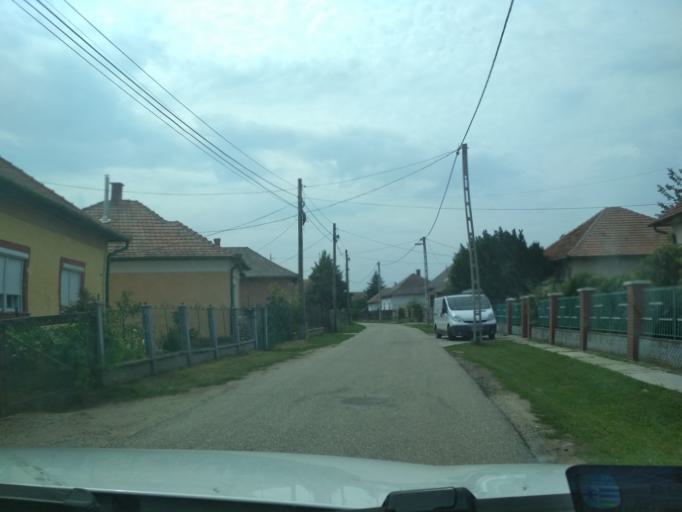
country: HU
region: Jasz-Nagykun-Szolnok
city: Tiszafured
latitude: 47.6151
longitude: 20.7536
